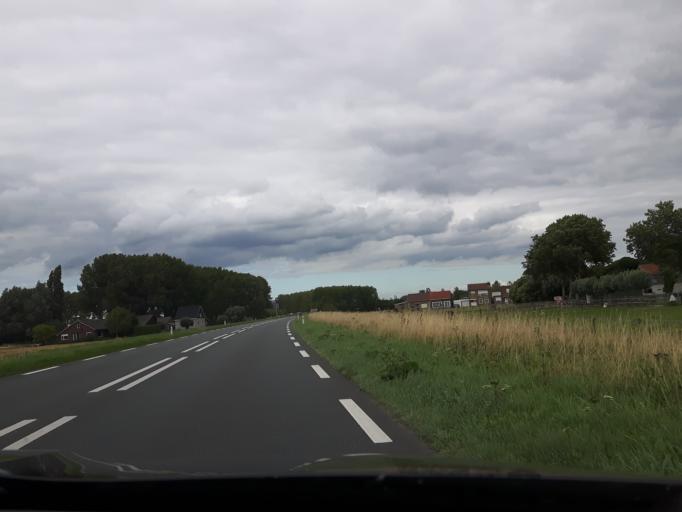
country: NL
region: Zeeland
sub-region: Gemeente Terneuzen
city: Sluiskil
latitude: 51.2862
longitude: 3.8293
